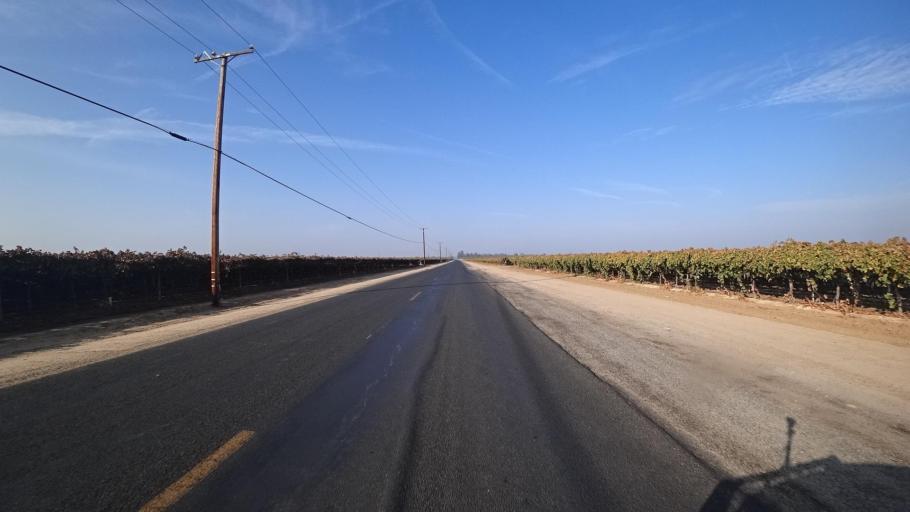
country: US
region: California
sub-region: Kern County
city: McFarland
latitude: 35.6746
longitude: -119.1992
